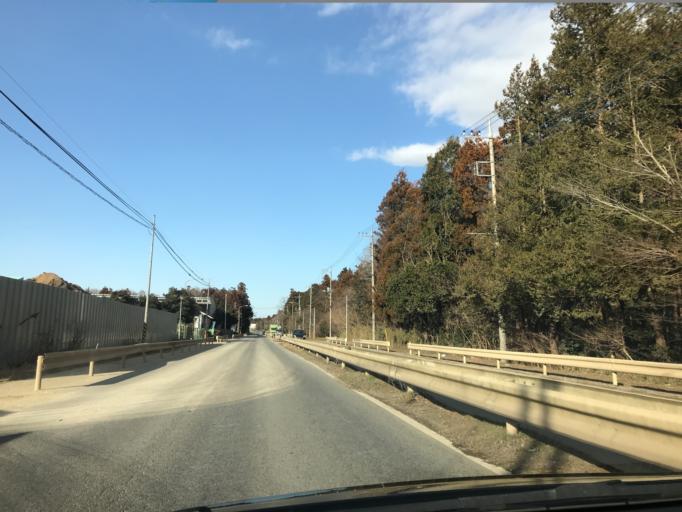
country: JP
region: Ibaraki
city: Ishige
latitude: 36.0978
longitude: 140.0364
